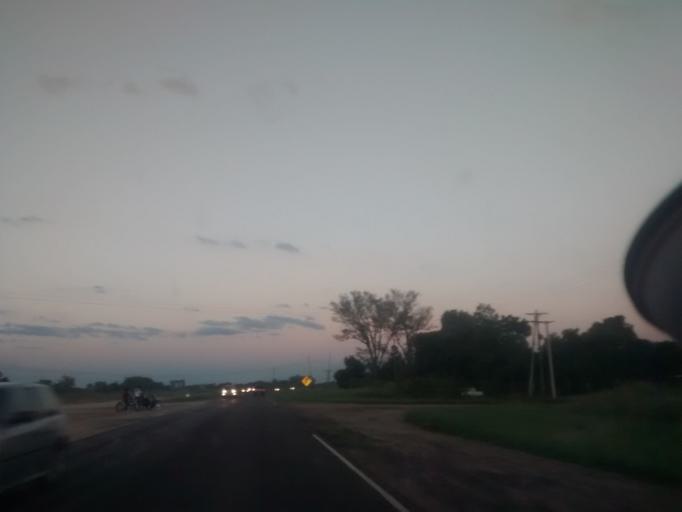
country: AR
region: Chaco
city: Makalle
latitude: -27.1915
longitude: -59.3012
